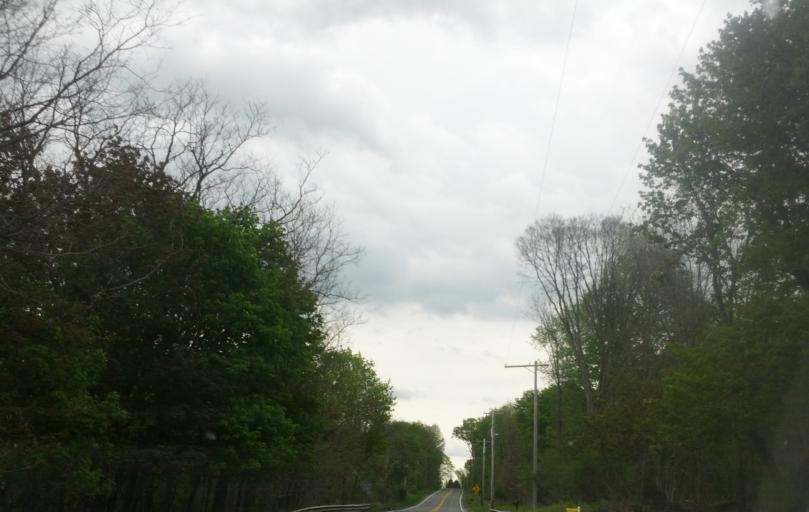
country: US
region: New York
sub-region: Onondaga County
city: Manlius
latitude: 42.9908
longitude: -76.0126
